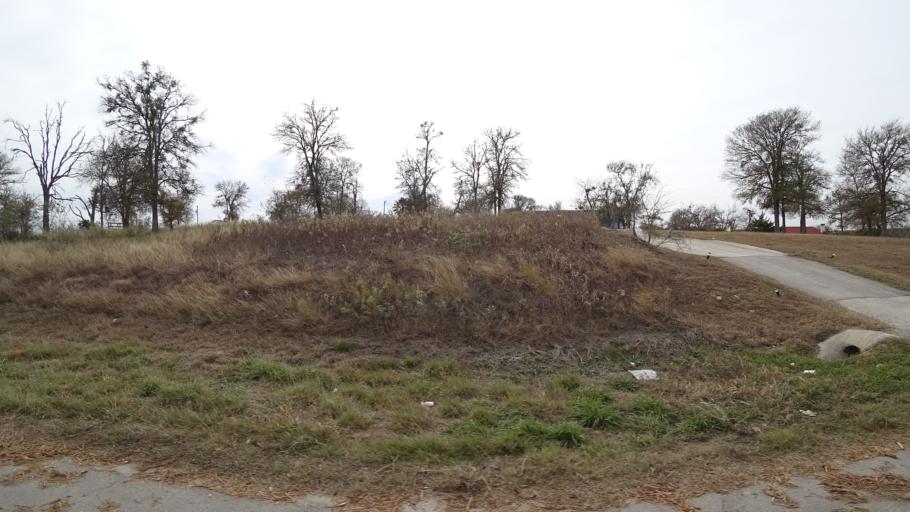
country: US
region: Texas
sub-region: Travis County
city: Garfield
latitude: 30.1489
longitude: -97.5805
